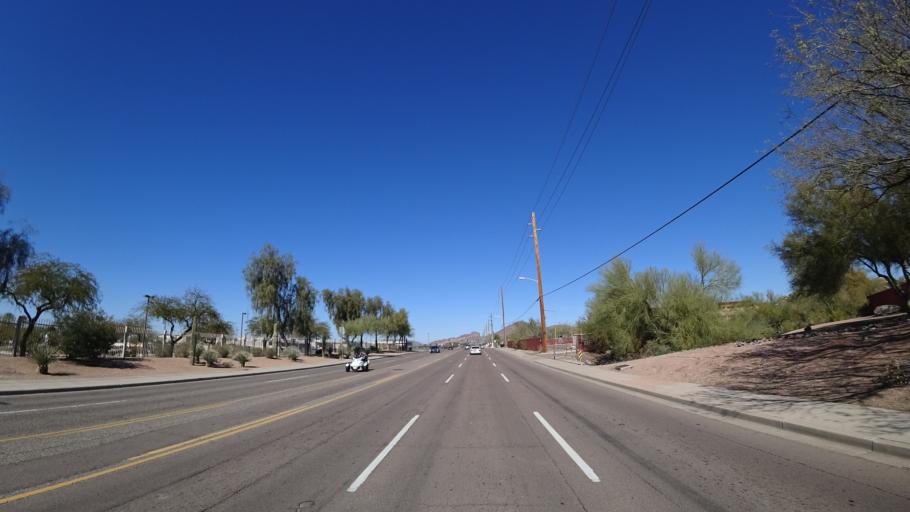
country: US
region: Arizona
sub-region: Maricopa County
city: Tempe Junction
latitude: 33.4589
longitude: -111.9698
